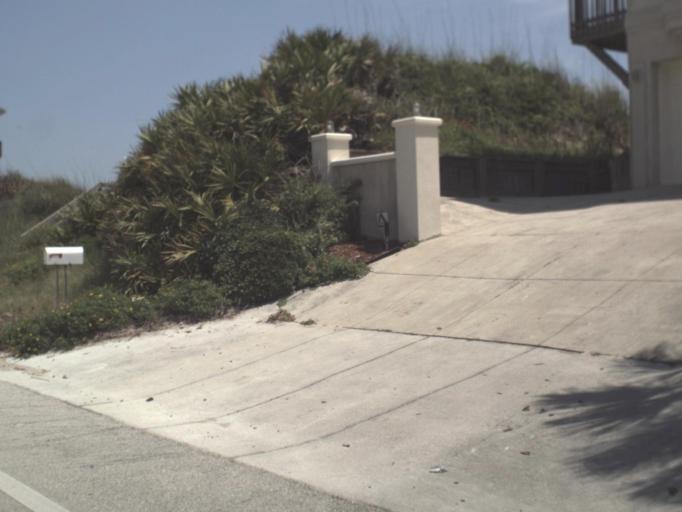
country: US
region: Florida
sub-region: Saint Johns County
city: Villano Beach
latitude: 29.9417
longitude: -81.3010
